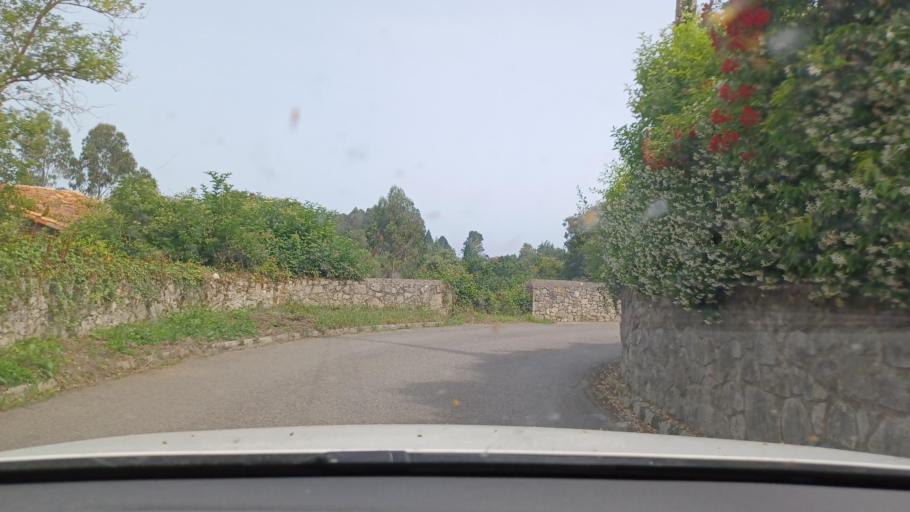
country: ES
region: Asturias
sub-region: Province of Asturias
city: Ribadesella
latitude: 43.4445
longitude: -4.9826
